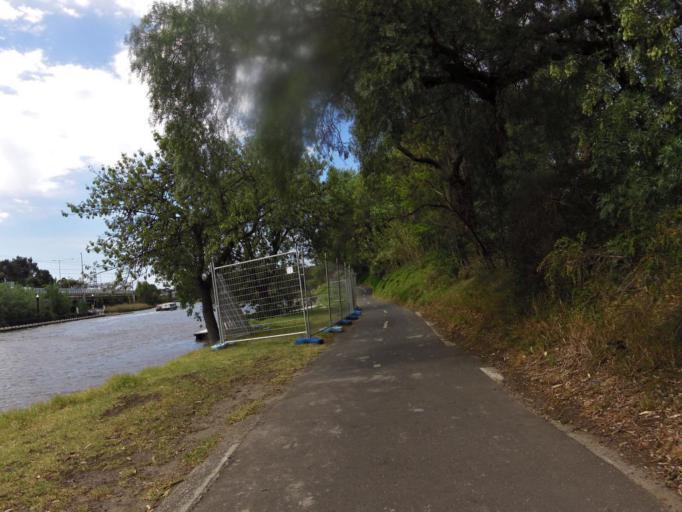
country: AU
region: Victoria
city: Albert Park
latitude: -37.8343
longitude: 144.9991
